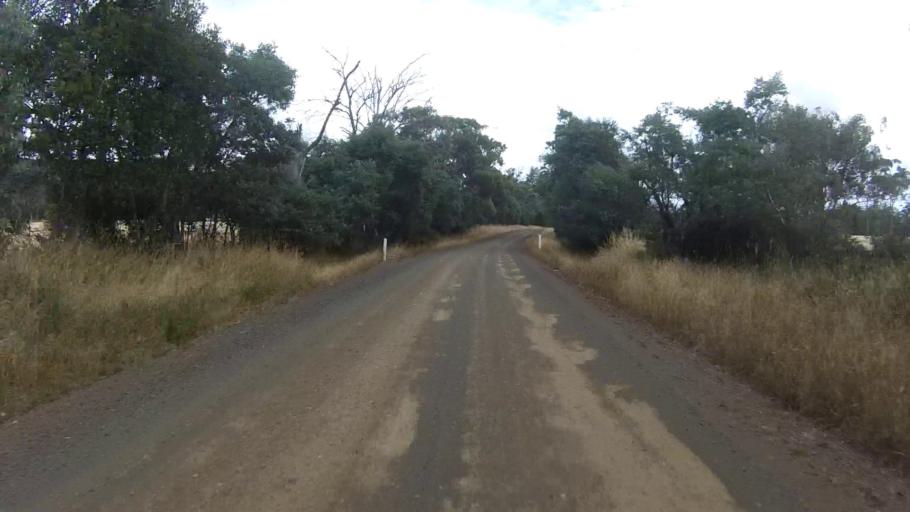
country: AU
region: Tasmania
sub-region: Break O'Day
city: St Helens
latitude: -41.8246
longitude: 147.9848
